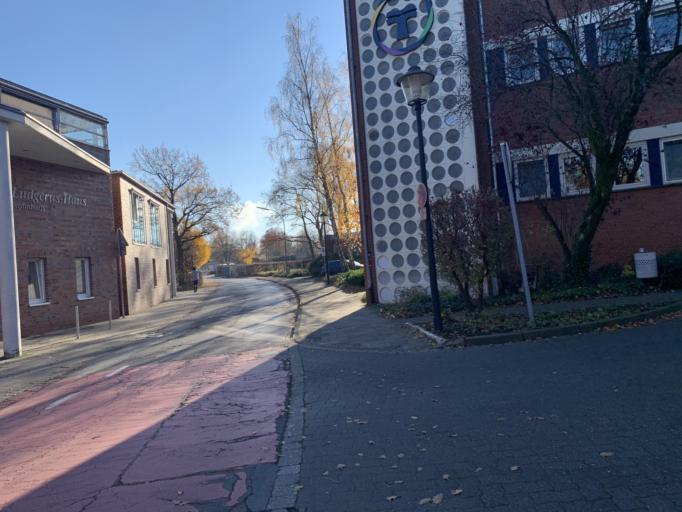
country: DE
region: North Rhine-Westphalia
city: Ludinghausen
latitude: 51.7694
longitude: 7.4478
